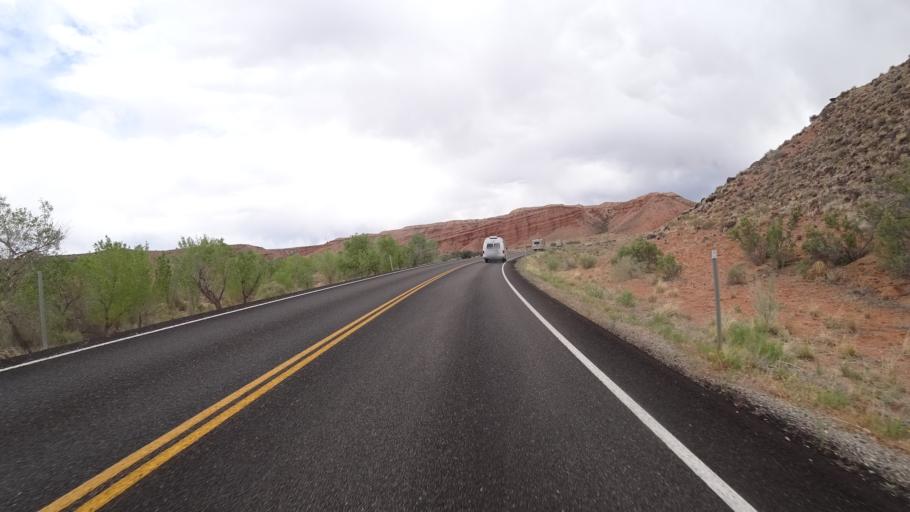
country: US
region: Utah
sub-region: Wayne County
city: Loa
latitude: 38.2861
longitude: -111.1396
